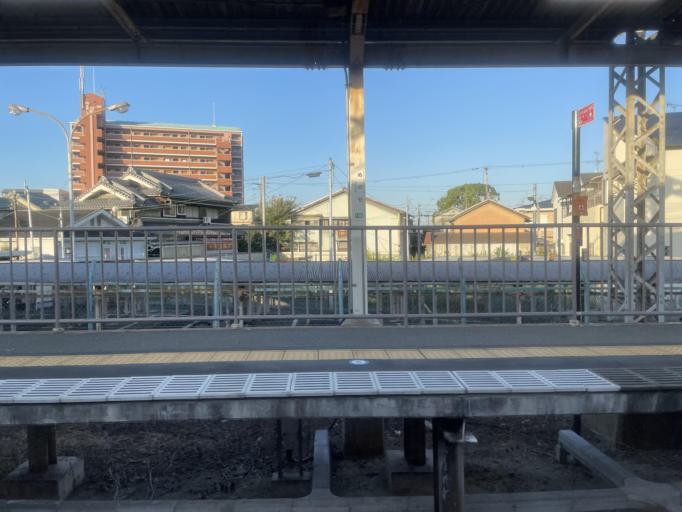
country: JP
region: Osaka
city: Matsubara
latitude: 34.5783
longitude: 135.5392
